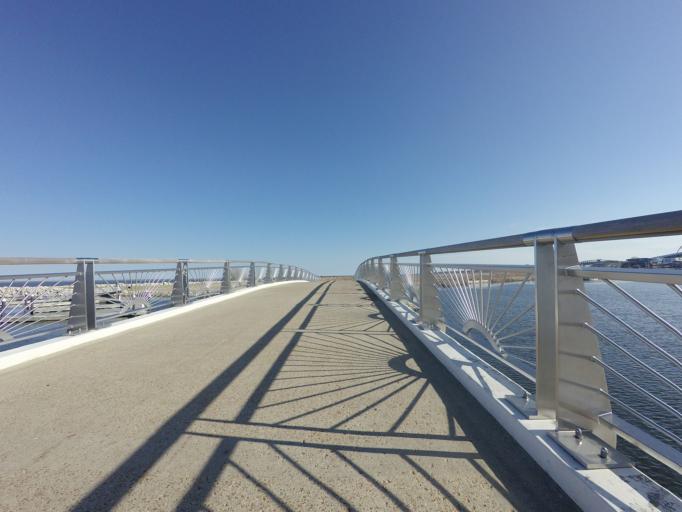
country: US
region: Wisconsin
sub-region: Milwaukee County
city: Milwaukee
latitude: 43.0343
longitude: -87.8965
